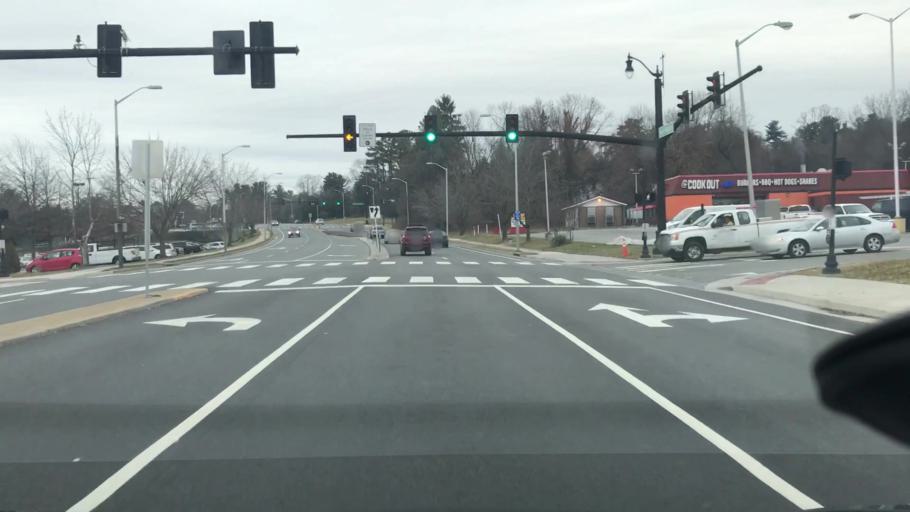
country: US
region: Virginia
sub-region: Montgomery County
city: Blacksburg
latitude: 37.2162
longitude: -80.4009
